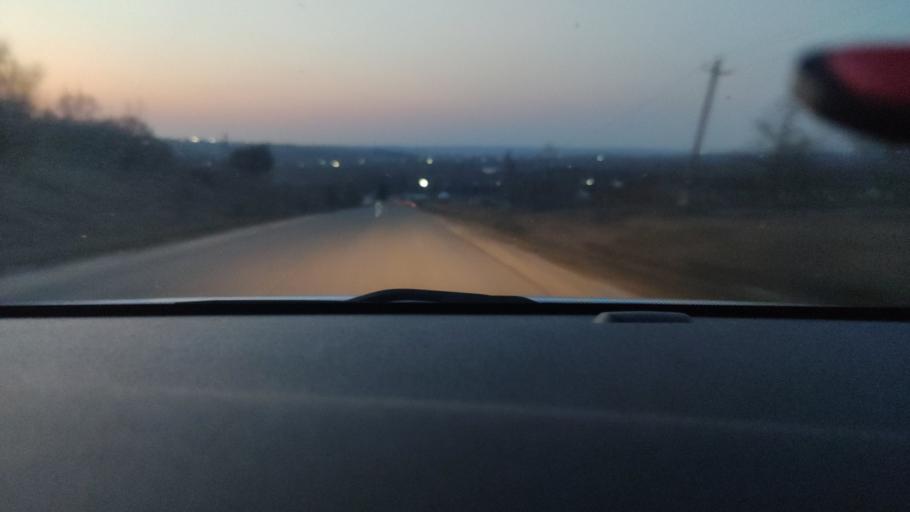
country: RU
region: Voronezj
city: Shilovo
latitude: 51.4555
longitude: 39.0245
